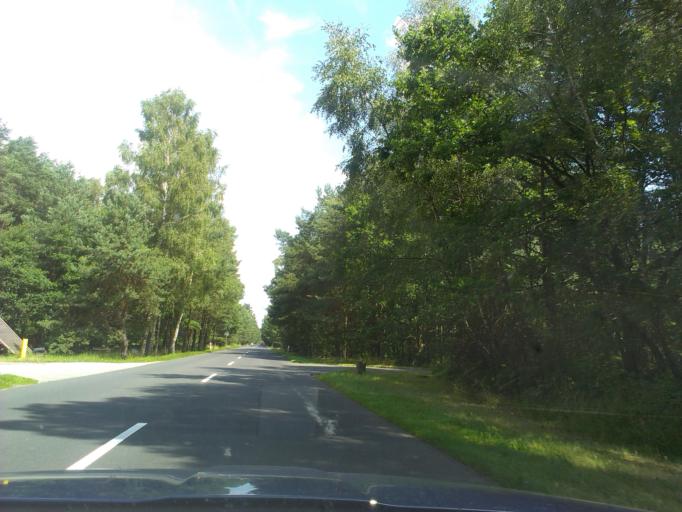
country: PL
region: West Pomeranian Voivodeship
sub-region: Swinoujscie
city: Swinoujscie
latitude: 53.8771
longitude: 14.3104
